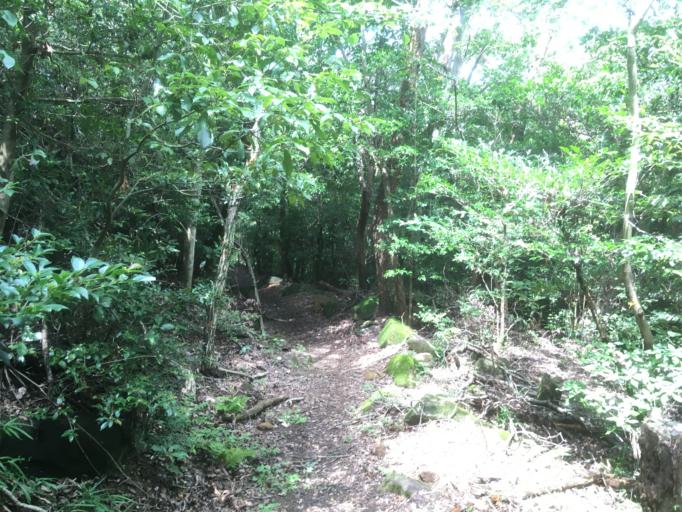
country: JP
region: Nara
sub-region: Ikoma-shi
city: Ikoma
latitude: 34.6794
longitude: 135.6851
